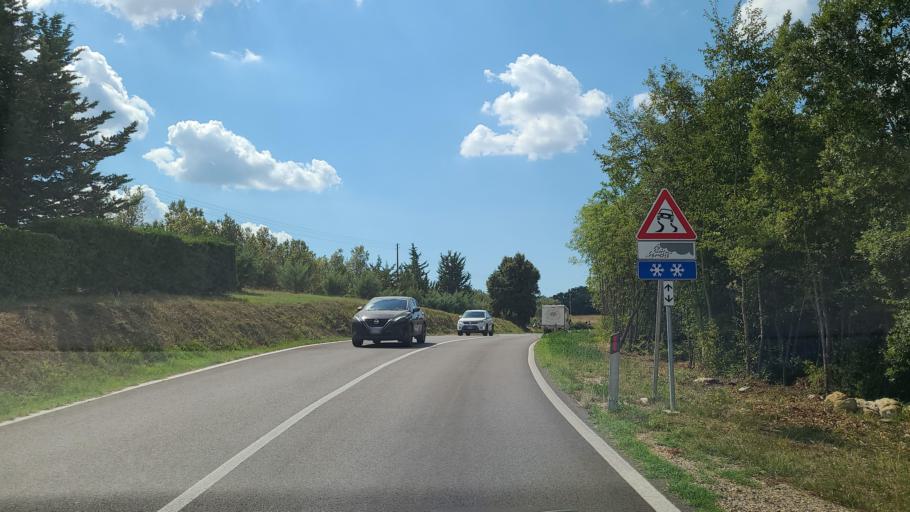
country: IT
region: Tuscany
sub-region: Provincia di Siena
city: Casole d'Elsa
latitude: 43.4030
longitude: 11.0367
